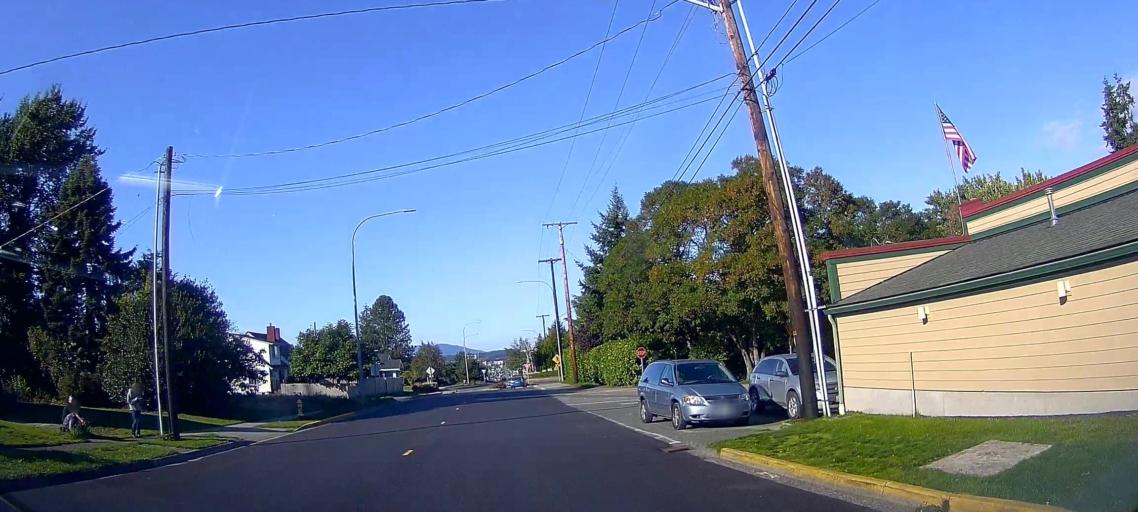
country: US
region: Washington
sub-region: Skagit County
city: Anacortes
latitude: 48.4923
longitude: -122.6129
